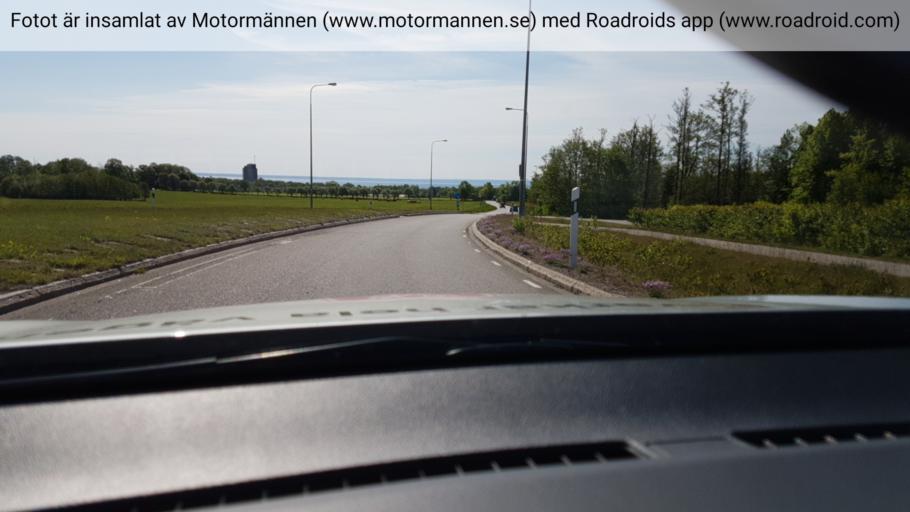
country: SE
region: Vaestra Goetaland
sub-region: Hjo Kommun
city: Hjo
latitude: 58.3206
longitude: 14.2685
